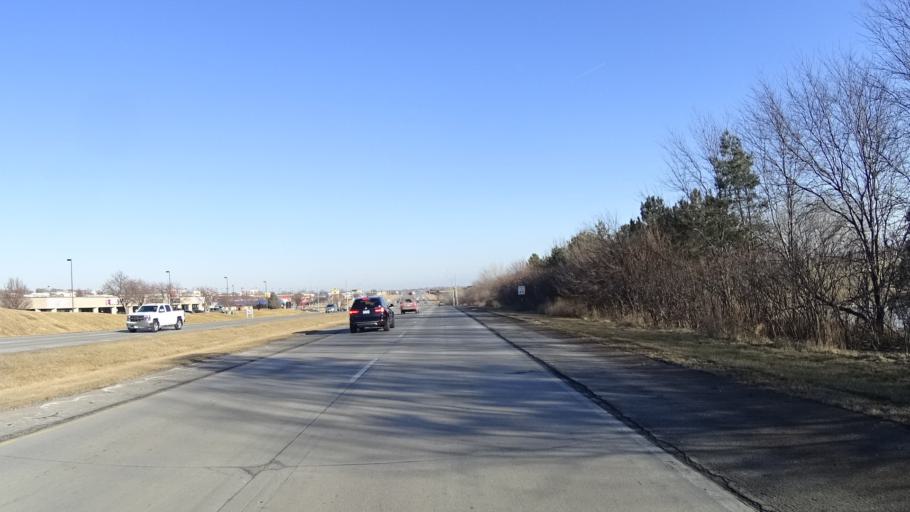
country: US
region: Nebraska
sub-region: Douglas County
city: Bennington
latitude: 41.2920
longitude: -96.1310
